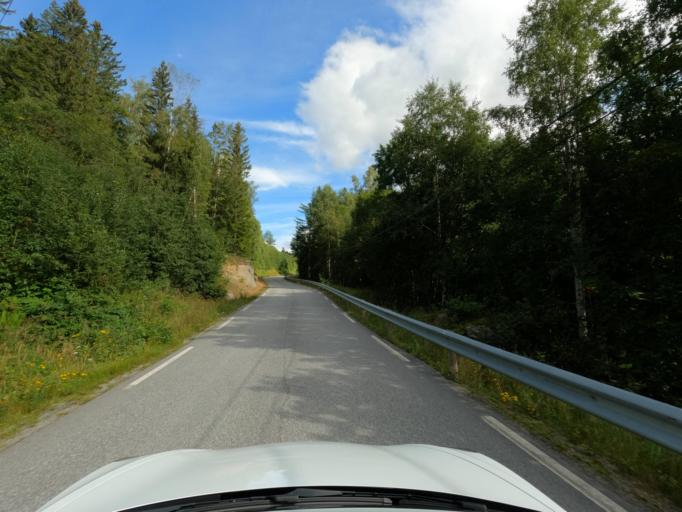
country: NO
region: Telemark
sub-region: Tinn
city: Rjukan
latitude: 60.0128
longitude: 8.7433
